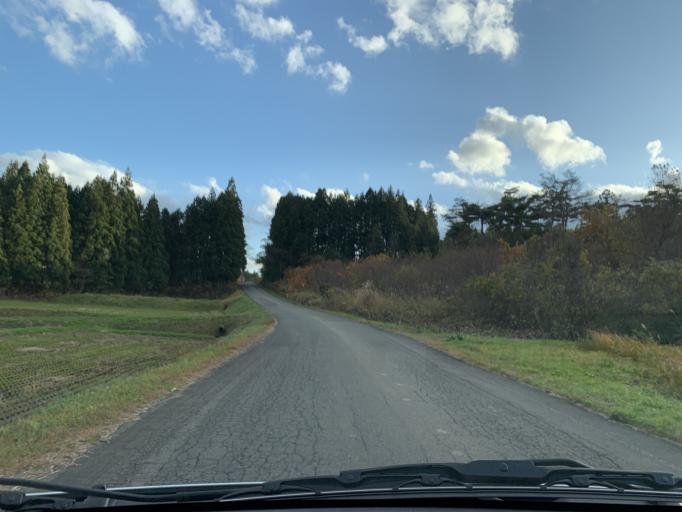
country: JP
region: Iwate
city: Mizusawa
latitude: 39.1138
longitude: 141.0001
